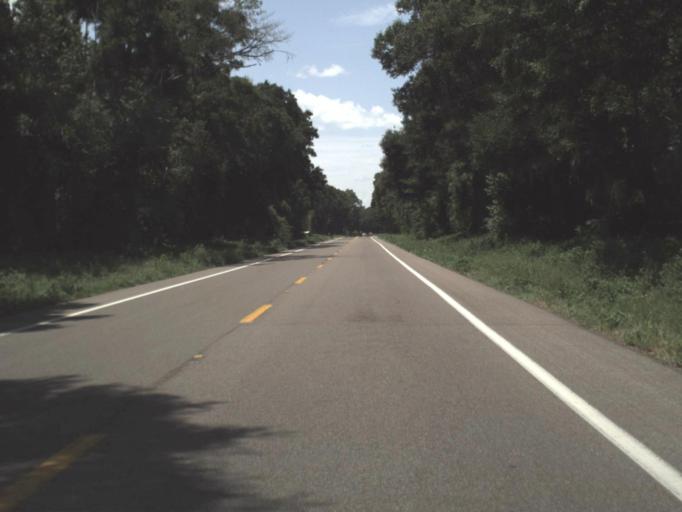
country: US
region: Florida
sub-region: Gilchrist County
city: Trenton
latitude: 29.6703
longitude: -82.8531
